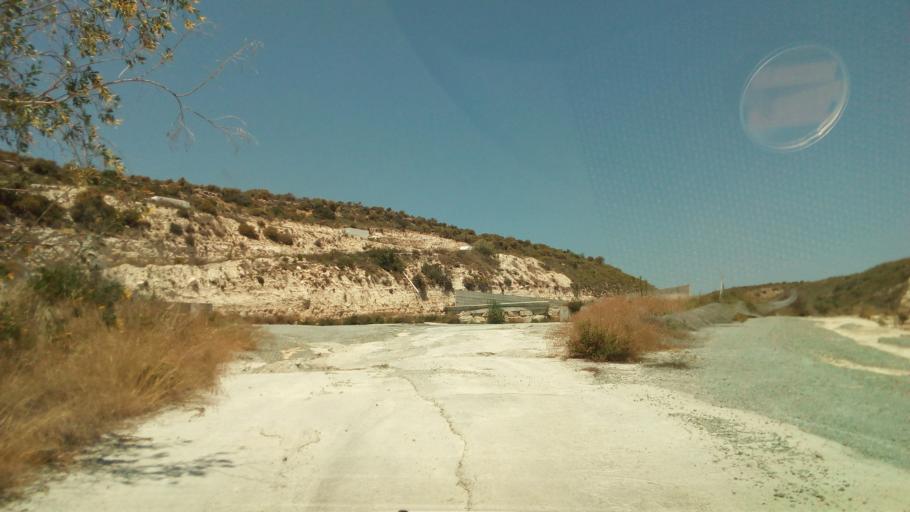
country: CY
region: Limassol
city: Ypsonas
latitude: 34.7309
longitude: 32.9568
